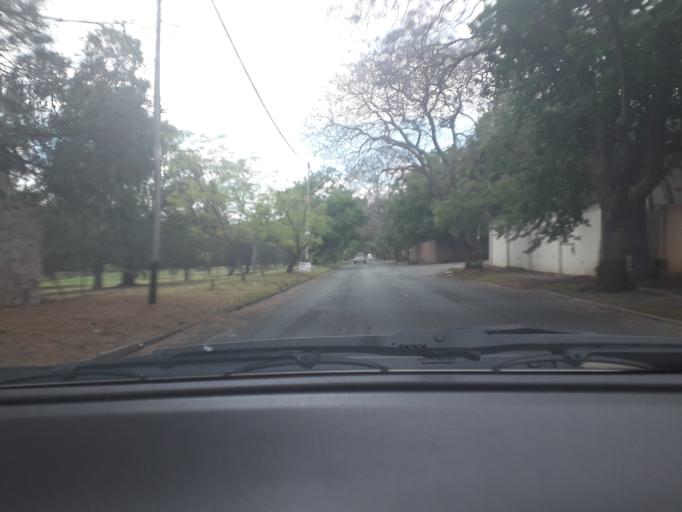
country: ZA
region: Gauteng
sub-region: City of Johannesburg Metropolitan Municipality
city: Johannesburg
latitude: -26.1599
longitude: 28.0199
